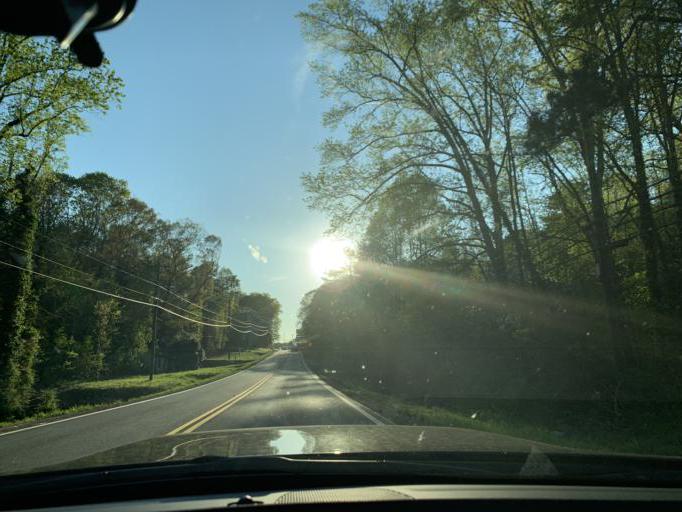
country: US
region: Georgia
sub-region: Forsyth County
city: Cumming
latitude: 34.2401
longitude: -84.1872
